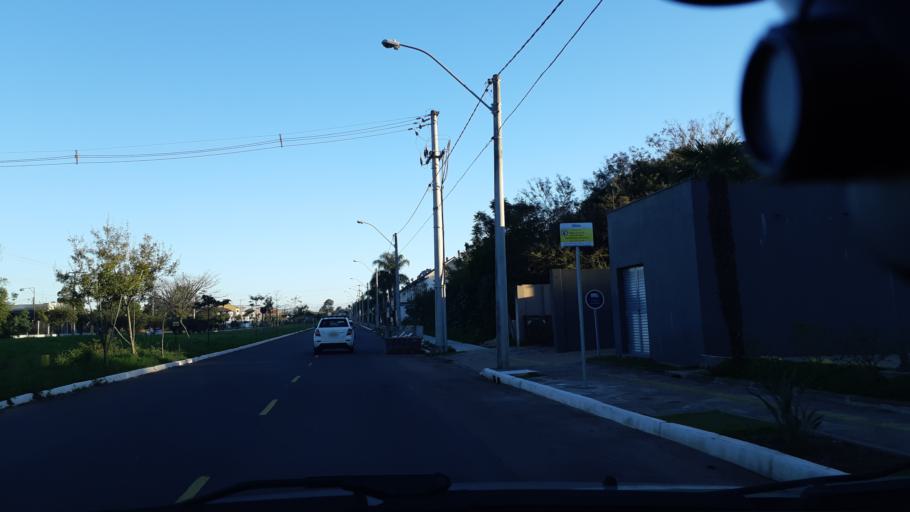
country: BR
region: Rio Grande do Sul
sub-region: Canoas
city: Canoas
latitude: -29.9194
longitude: -51.1552
